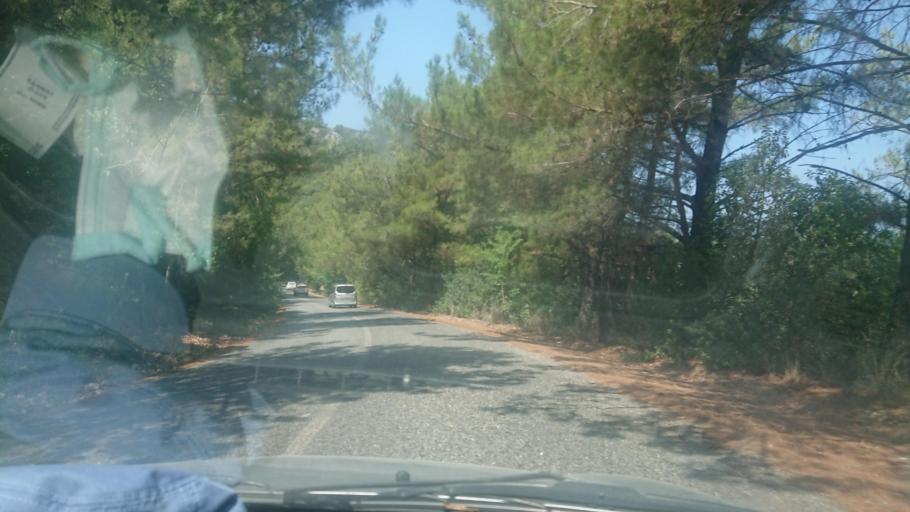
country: TR
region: Aydin
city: Atburgazi
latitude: 37.6976
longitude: 27.1740
